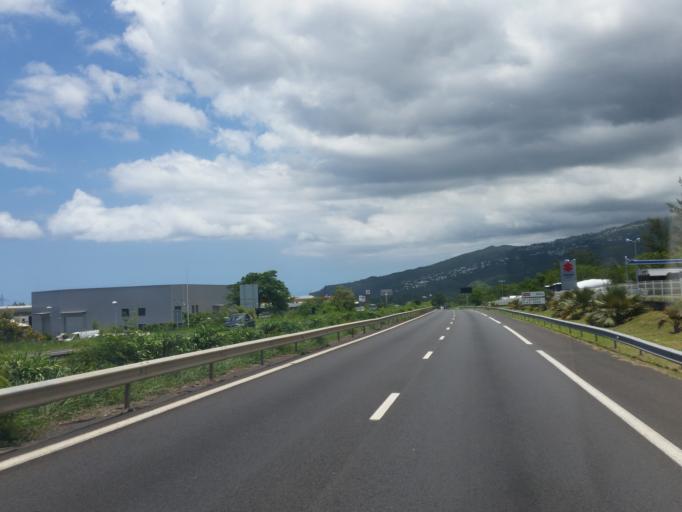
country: RE
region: Reunion
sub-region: Reunion
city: La Possession
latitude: -20.9520
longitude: 55.3175
